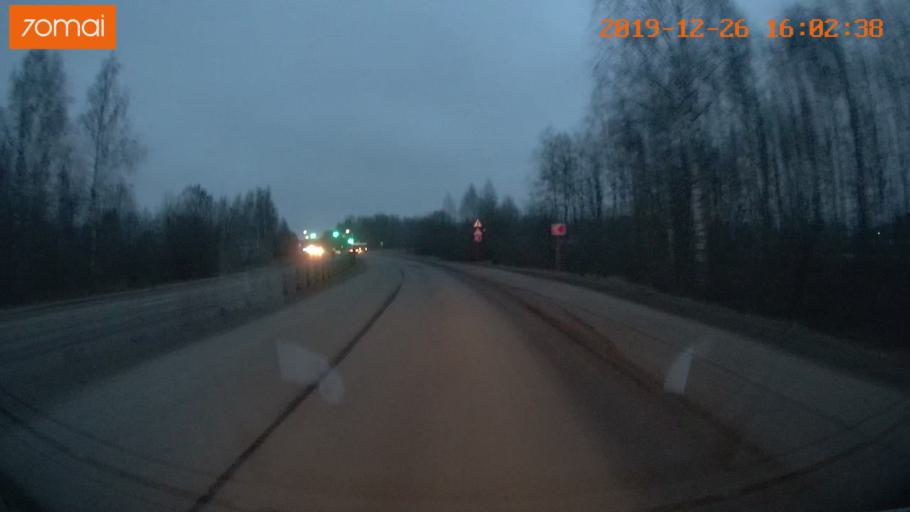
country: RU
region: Jaroslavl
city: Rybinsk
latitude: 58.0105
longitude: 38.8389
